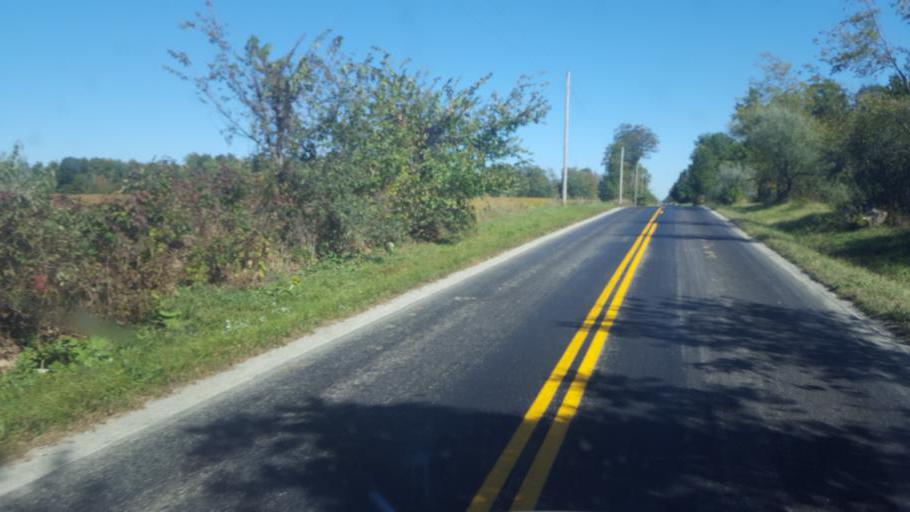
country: US
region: Ohio
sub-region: Wayne County
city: West Salem
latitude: 40.9920
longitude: -82.1984
